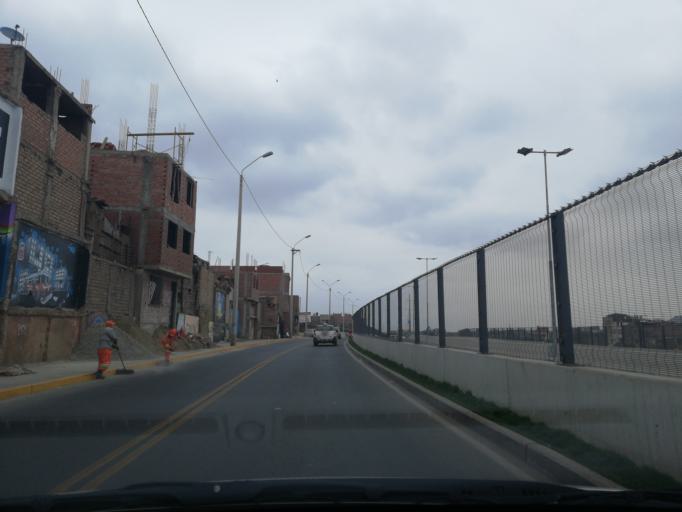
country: PE
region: Lima
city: Lima
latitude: -12.0369
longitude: -77.0569
